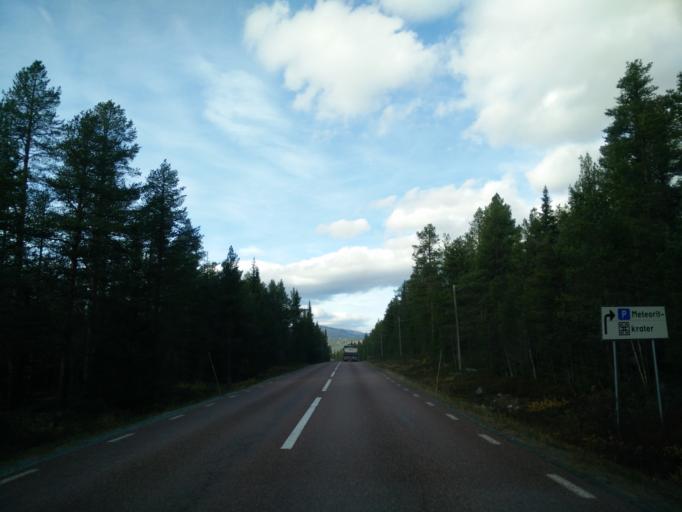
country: NO
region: Hedmark
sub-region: Engerdal
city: Engerdal
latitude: 62.4993
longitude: 12.6290
